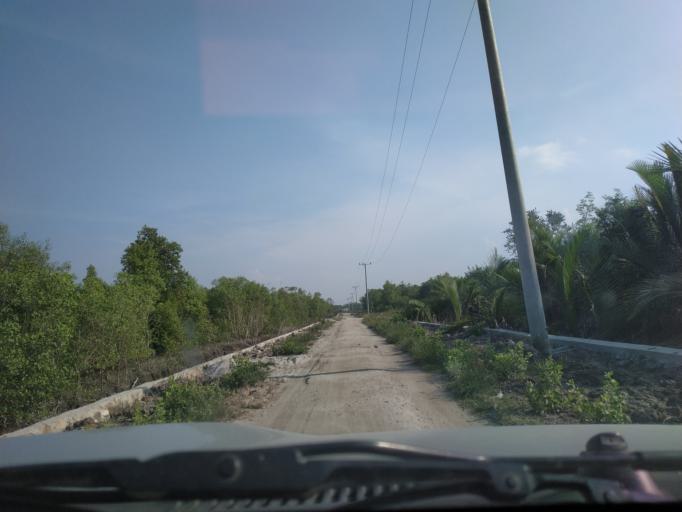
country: ID
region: North Sumatra
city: Teluk Nibung
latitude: 3.1059
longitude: 99.7780
